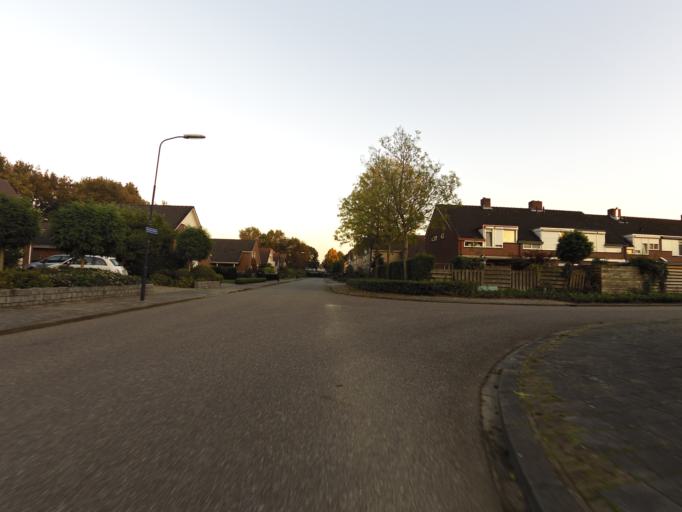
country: NL
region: Gelderland
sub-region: Oude IJsselstreek
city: Gendringen
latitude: 51.9249
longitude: 6.3408
